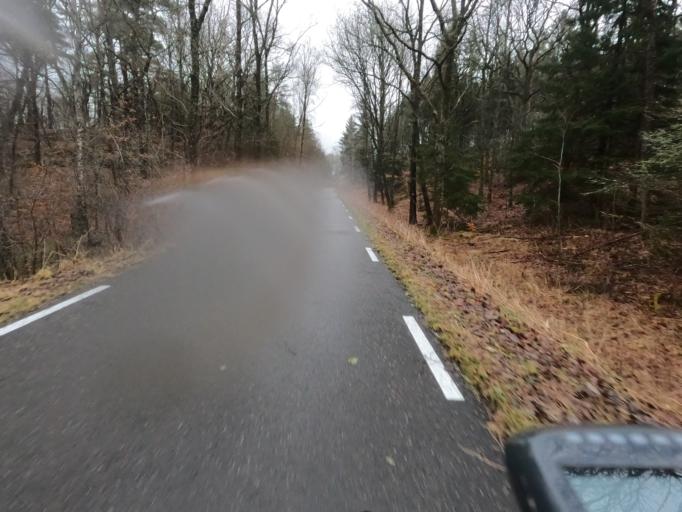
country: SE
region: Halland
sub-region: Halmstads Kommun
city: Aled
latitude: 56.7016
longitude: 13.0224
